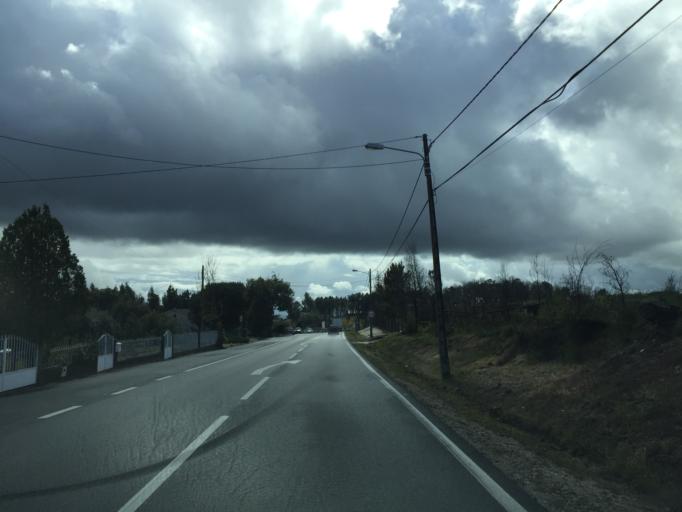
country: PT
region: Coimbra
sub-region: Oliveira do Hospital
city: Oliveira do Hospital
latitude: 40.3285
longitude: -7.8735
